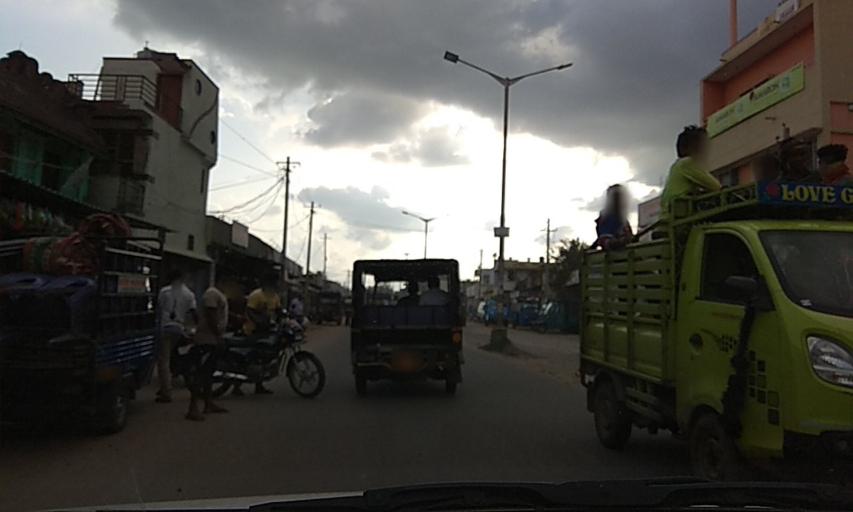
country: IN
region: Karnataka
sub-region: Chamrajnagar
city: Gundlupet
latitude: 11.8079
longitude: 76.6936
